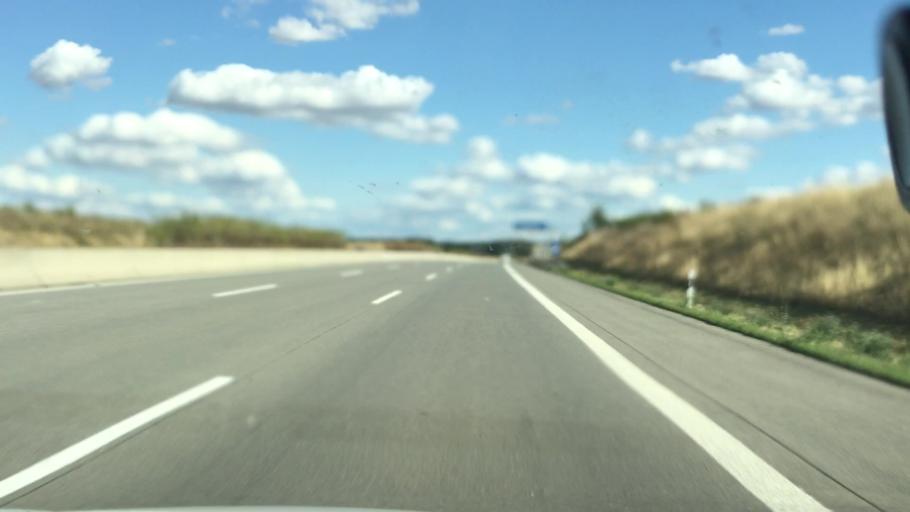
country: DE
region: Thuringia
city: Vollmershain
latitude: 50.8599
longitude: 12.3063
